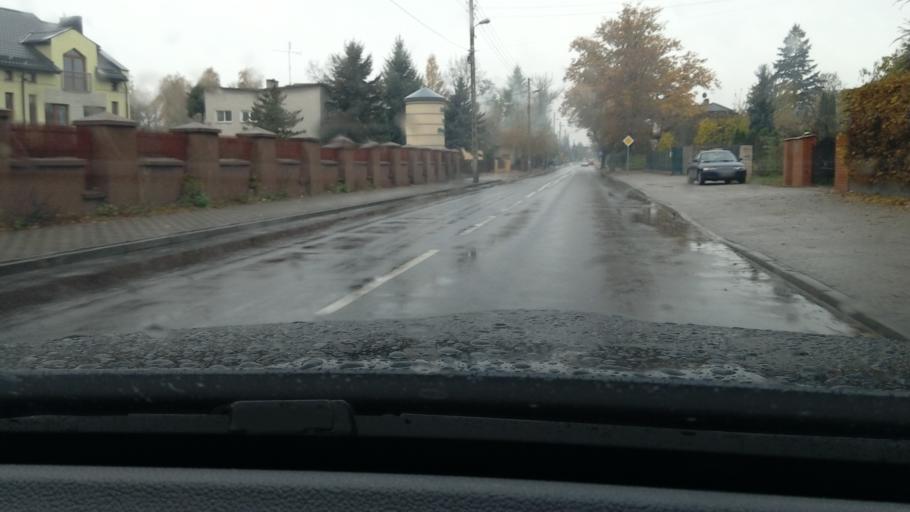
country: PL
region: Lodz Voivodeship
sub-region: Skierniewice
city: Skierniewice
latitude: 51.9559
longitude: 20.1349
